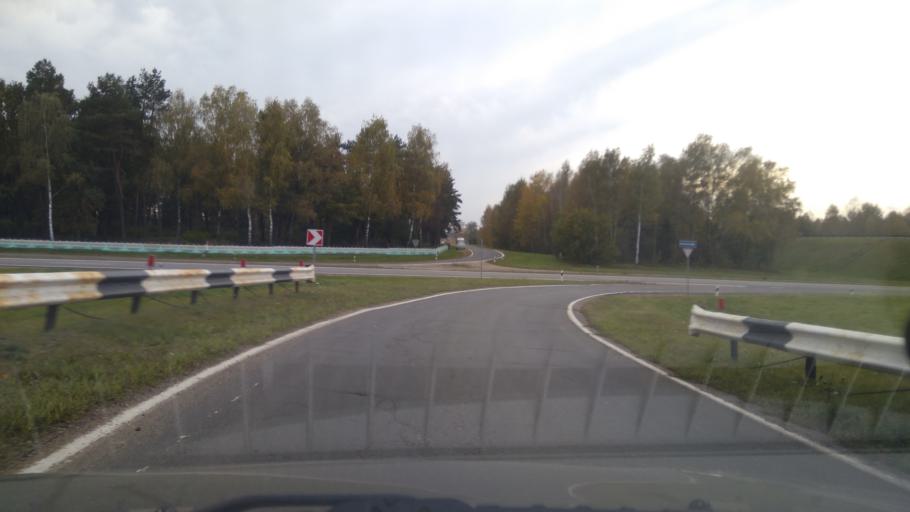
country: BY
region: Minsk
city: Dukora
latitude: 53.6600
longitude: 27.9505
